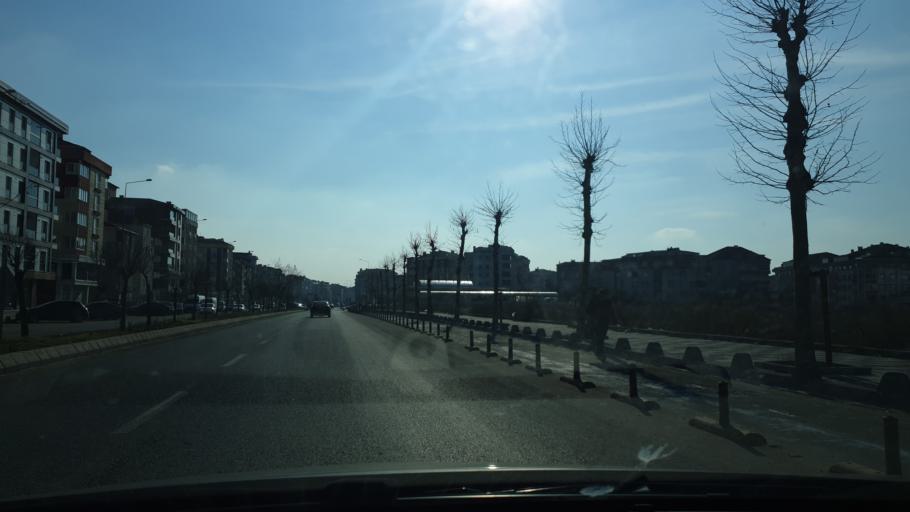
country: TR
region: Tekirdag
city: Cerkezkoey
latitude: 41.2906
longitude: 27.9926
